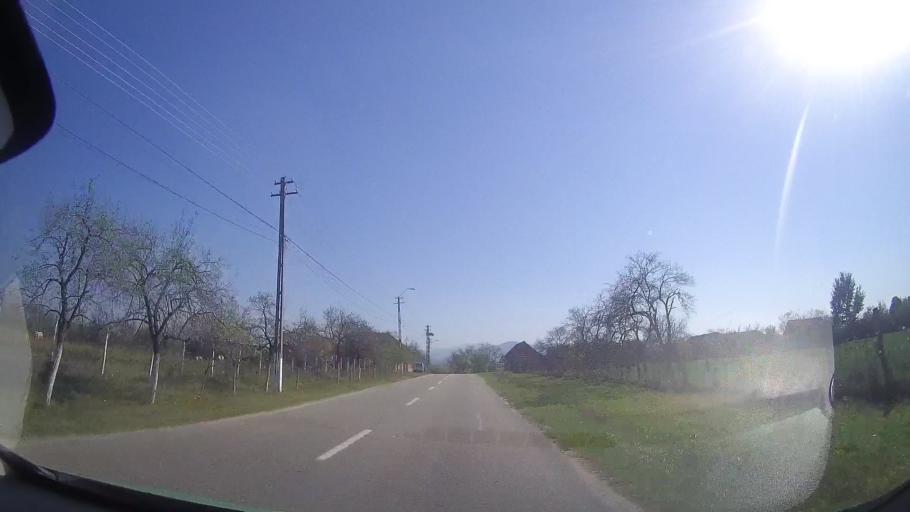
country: RO
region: Timis
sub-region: Comuna Traian Vuia
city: Traian Vuia
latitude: 45.7878
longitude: 22.0324
